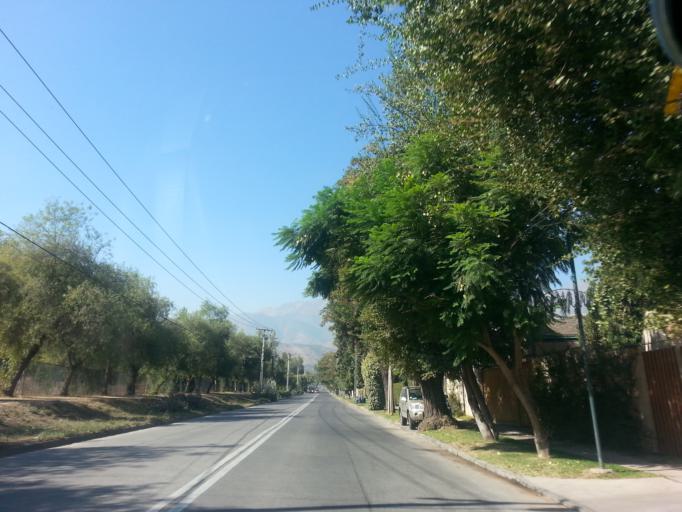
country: CL
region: Santiago Metropolitan
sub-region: Provincia de Santiago
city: Villa Presidente Frei, Nunoa, Santiago, Chile
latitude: -33.4346
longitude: -70.5478
